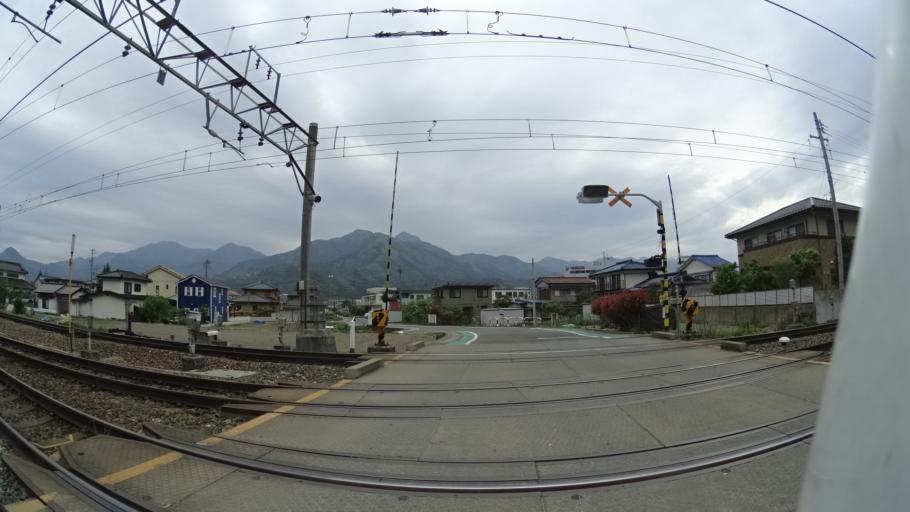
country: JP
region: Nagano
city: Nagano-shi
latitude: 36.4957
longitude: 138.1521
